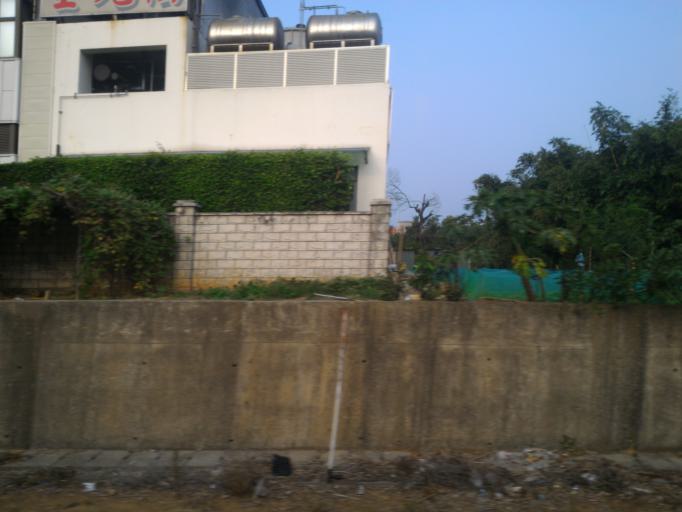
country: TW
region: Taiwan
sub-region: Taoyuan
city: Taoyuan
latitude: 24.9495
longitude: 121.3375
